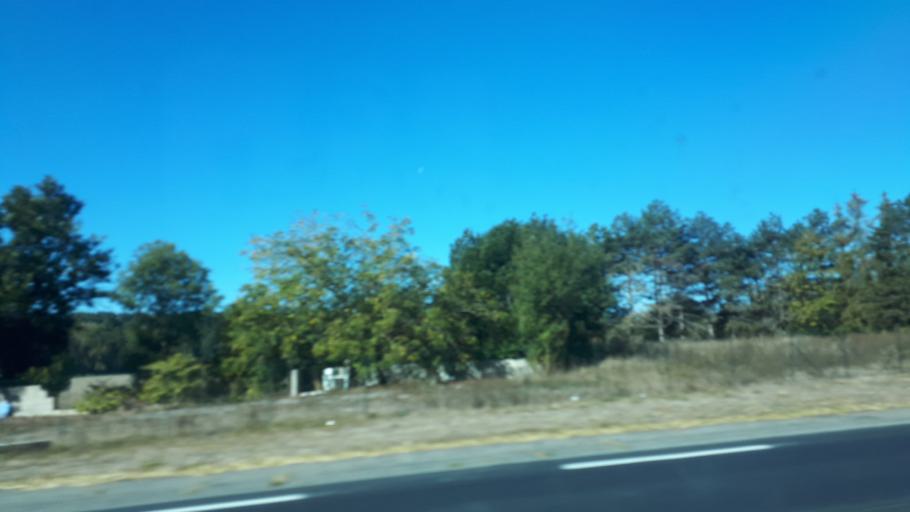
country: FR
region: Centre
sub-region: Departement d'Eure-et-Loir
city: Marboue
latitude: 48.0995
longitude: 1.3301
